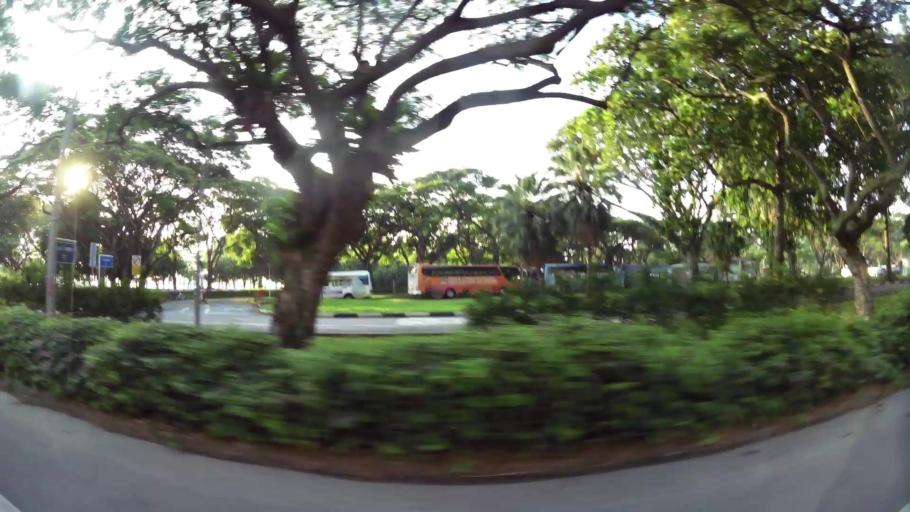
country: SG
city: Singapore
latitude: 1.3077
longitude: 103.9304
